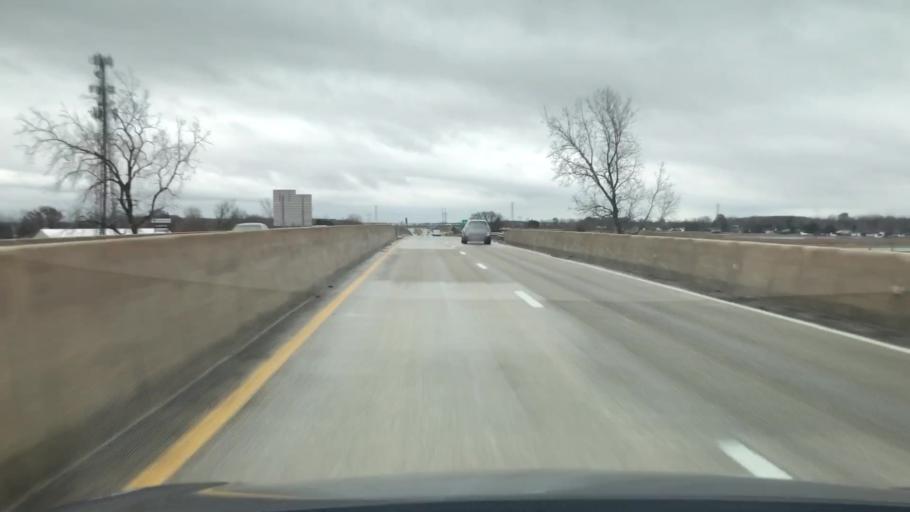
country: US
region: Ohio
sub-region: Wood County
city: Northwood
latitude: 41.5990
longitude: -83.4769
